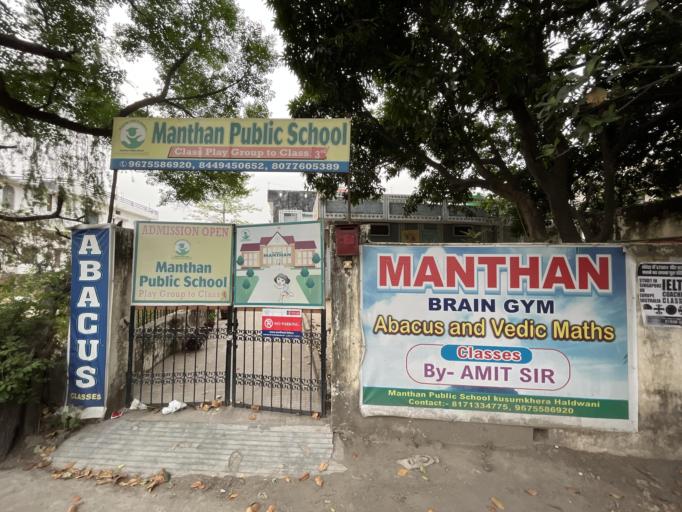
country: IN
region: Uttarakhand
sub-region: Naini Tal
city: Haldwani
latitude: 29.2213
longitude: 79.5036
